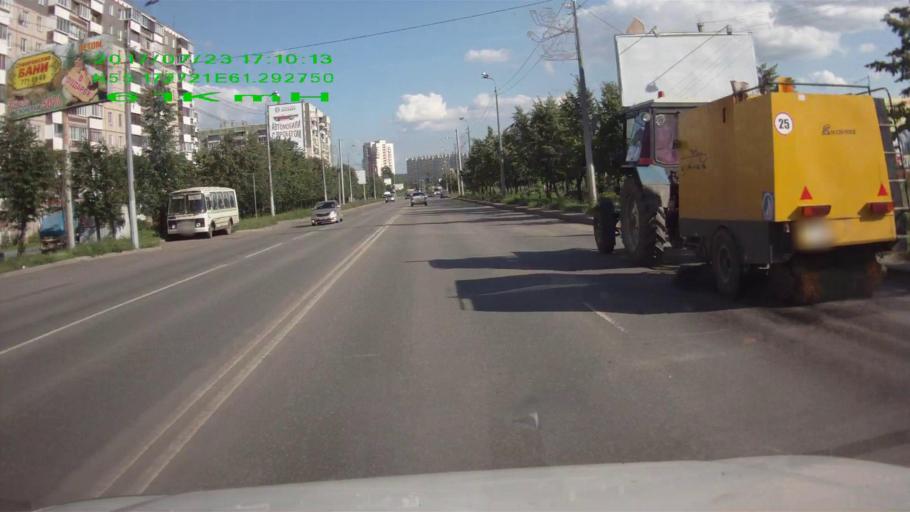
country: RU
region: Chelyabinsk
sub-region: Gorod Chelyabinsk
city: Chelyabinsk
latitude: 55.1725
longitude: 61.2931
